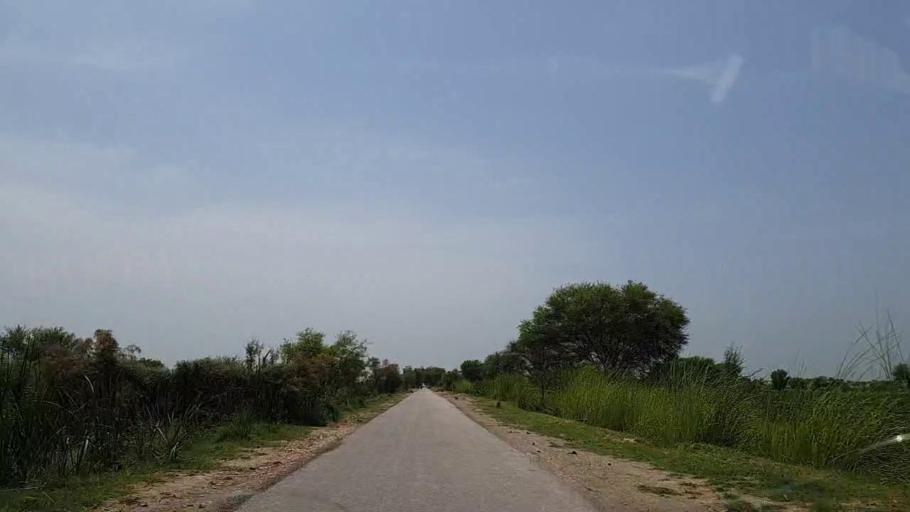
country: PK
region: Sindh
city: Khanpur
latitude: 27.8915
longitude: 69.4955
